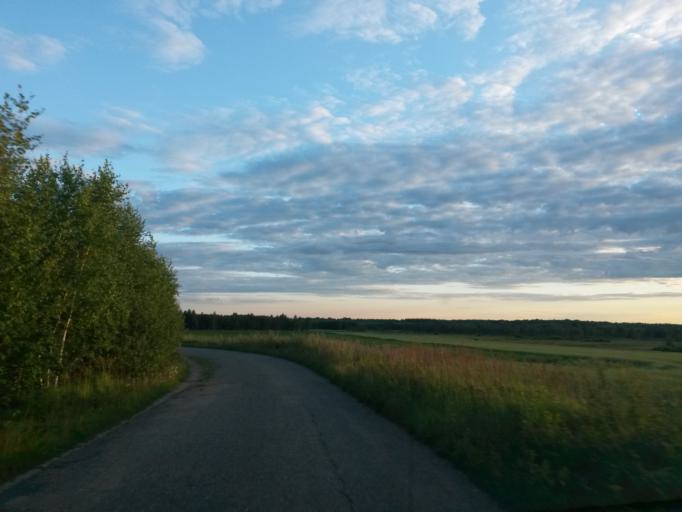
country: RU
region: Jaroslavl
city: Gavrilov-Yam
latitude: 57.3392
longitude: 40.0373
